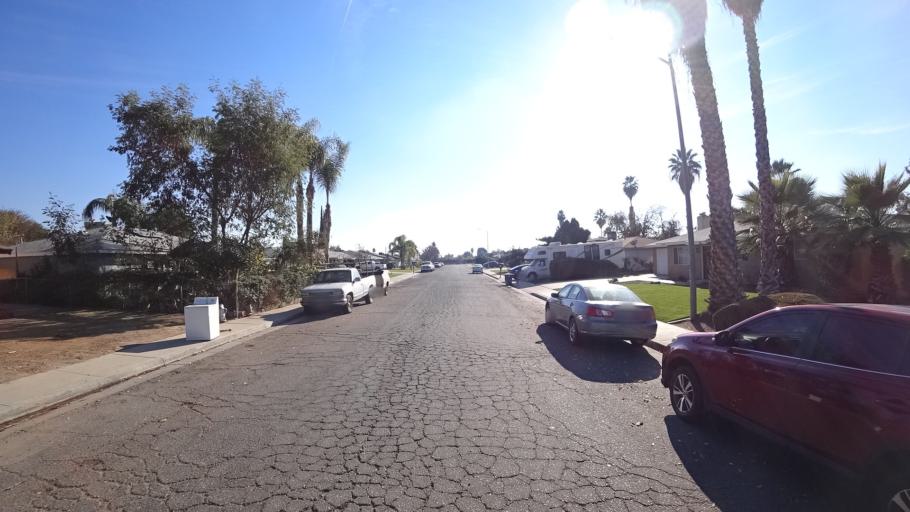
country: US
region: California
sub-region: Kern County
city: Greenfield
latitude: 35.3020
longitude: -119.0509
